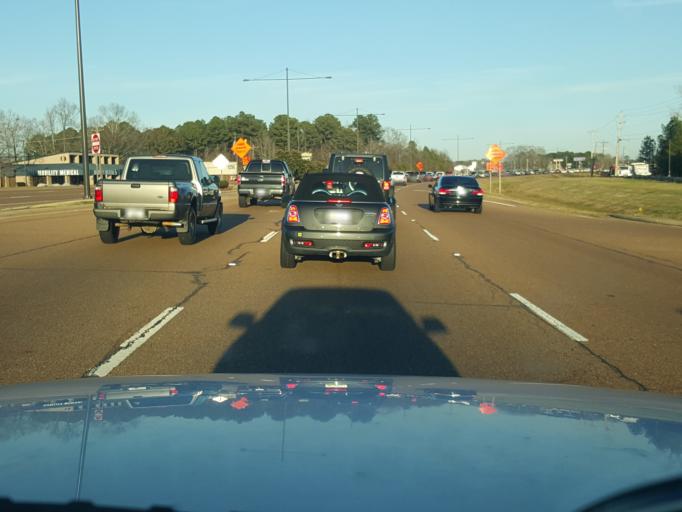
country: US
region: Mississippi
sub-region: Rankin County
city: Flowood
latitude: 32.3391
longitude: -90.0903
